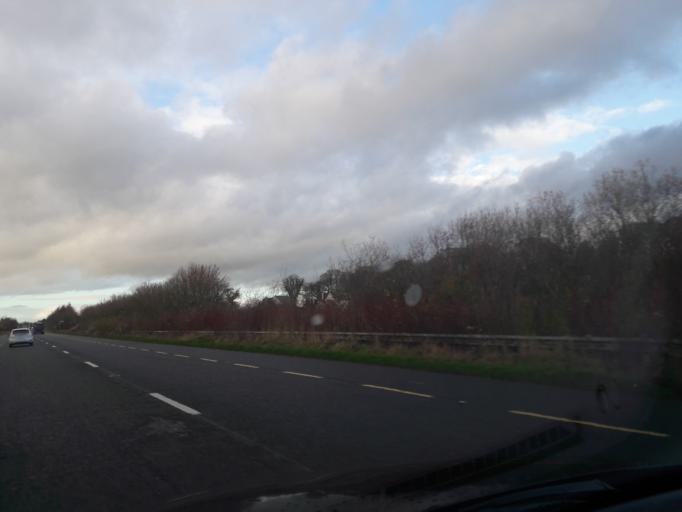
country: IE
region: Leinster
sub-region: Lu
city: Ardee
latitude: 53.8799
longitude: -6.5647
